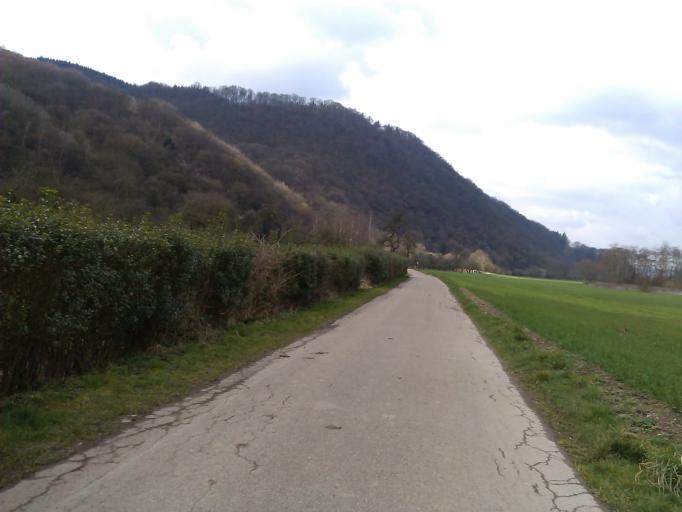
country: DE
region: Rheinland-Pfalz
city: Hammerstein
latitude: 50.4603
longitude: 7.3530
